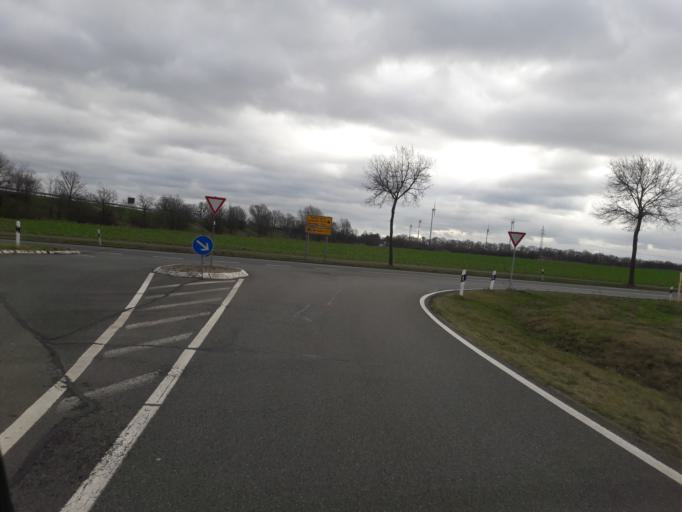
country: DE
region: Lower Saxony
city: Uchte
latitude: 52.4888
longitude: 8.8882
